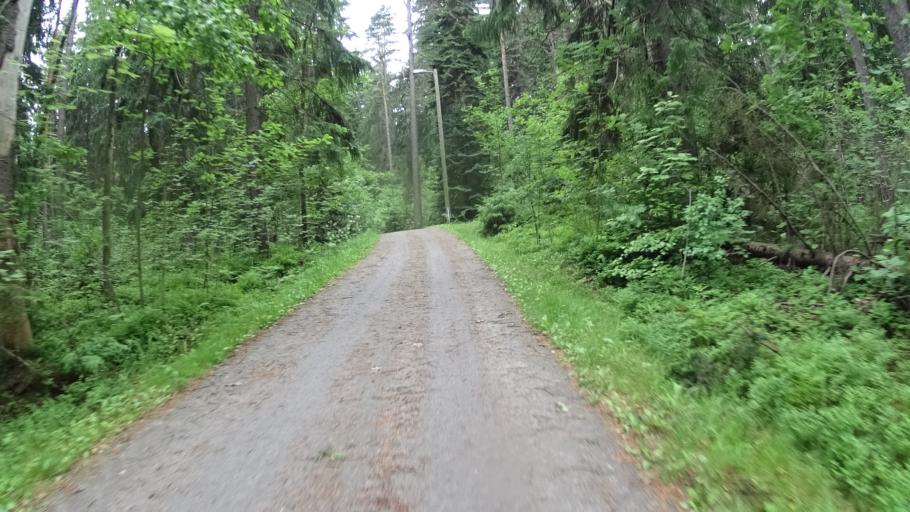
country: FI
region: Uusimaa
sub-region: Helsinki
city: Helsinki
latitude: 60.2700
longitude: 24.9355
